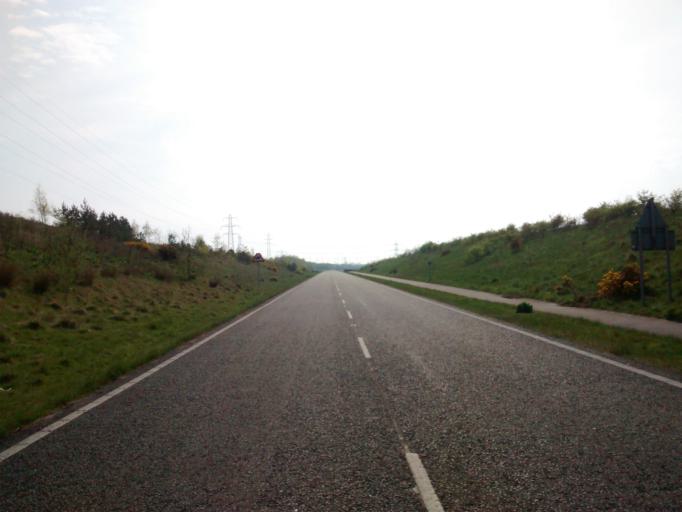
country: GB
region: England
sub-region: County Durham
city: South Hetton
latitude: 54.8075
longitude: -1.3804
